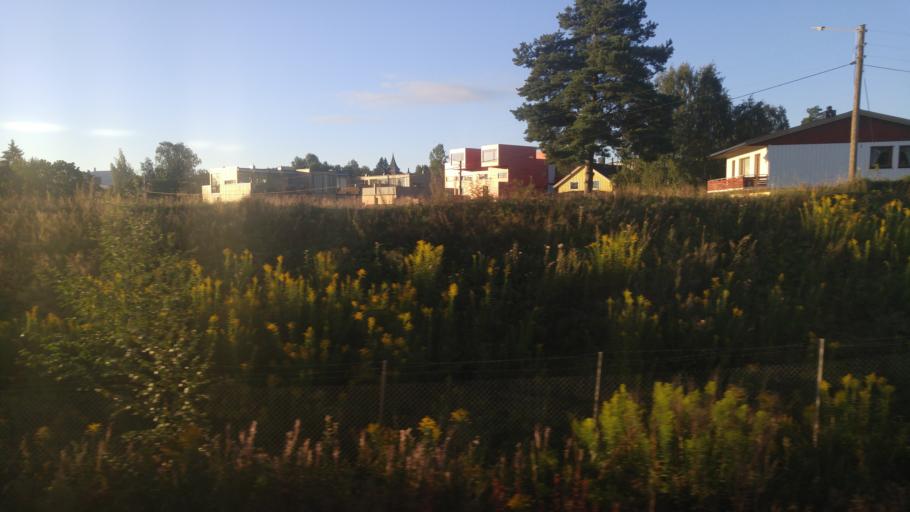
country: NO
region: Akershus
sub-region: Skedsmo
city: Lillestrom
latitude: 59.9559
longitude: 11.0109
